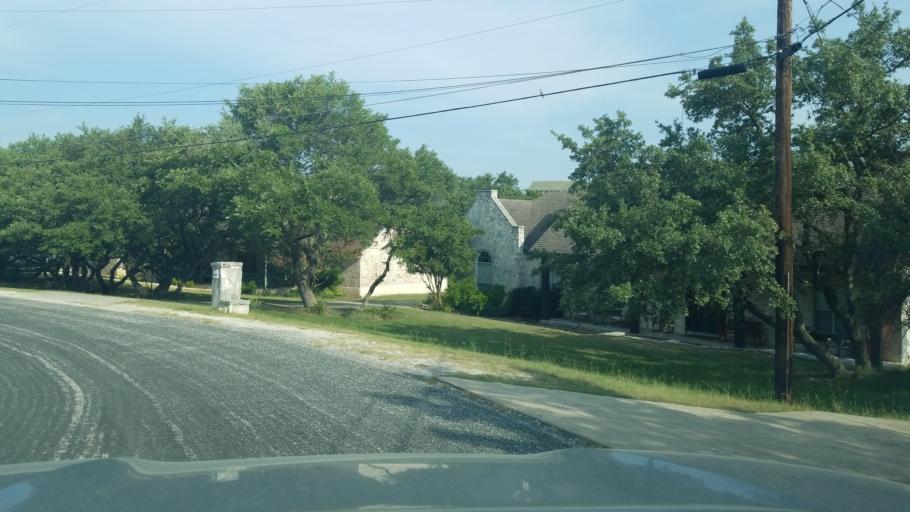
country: US
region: Texas
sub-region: Bexar County
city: Timberwood Park
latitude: 29.7026
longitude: -98.4942
